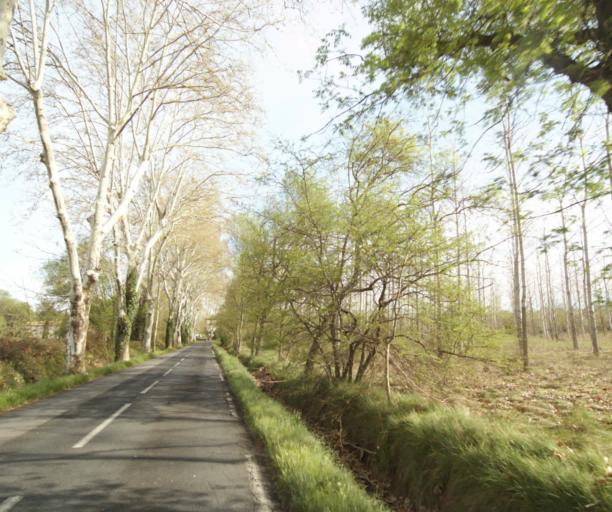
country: FR
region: Languedoc-Roussillon
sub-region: Departement de l'Herault
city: Laverune
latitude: 43.5894
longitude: 3.8186
